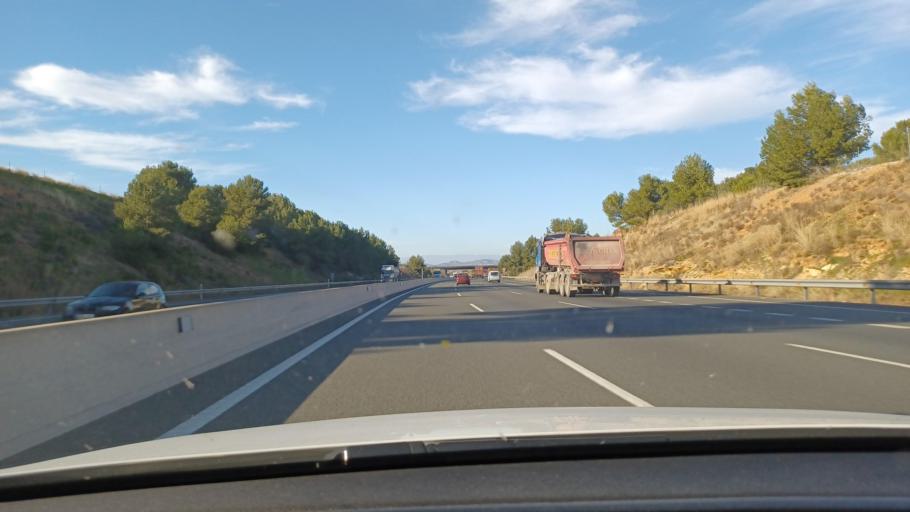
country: ES
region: Valencia
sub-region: Provincia de Valencia
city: Torrent
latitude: 39.4039
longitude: -0.4950
